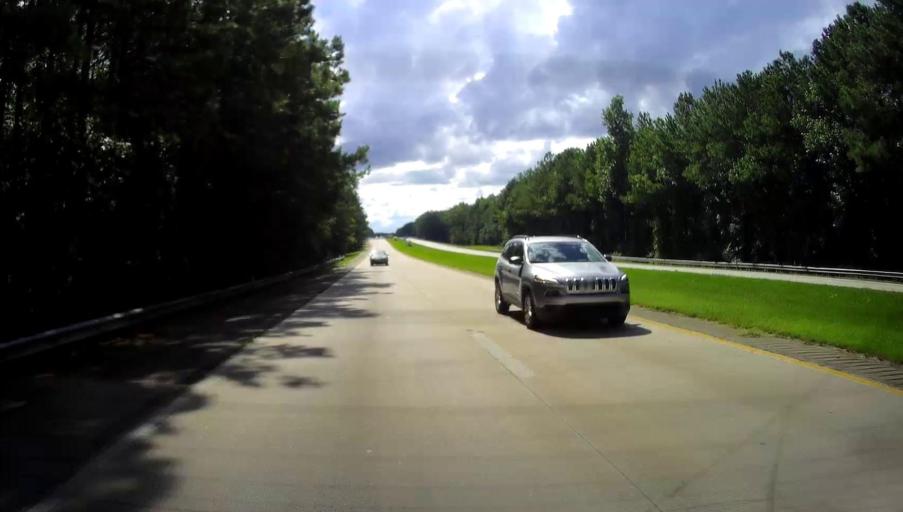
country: US
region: Georgia
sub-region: Muscogee County
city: Columbus
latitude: 32.5555
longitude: -84.8862
